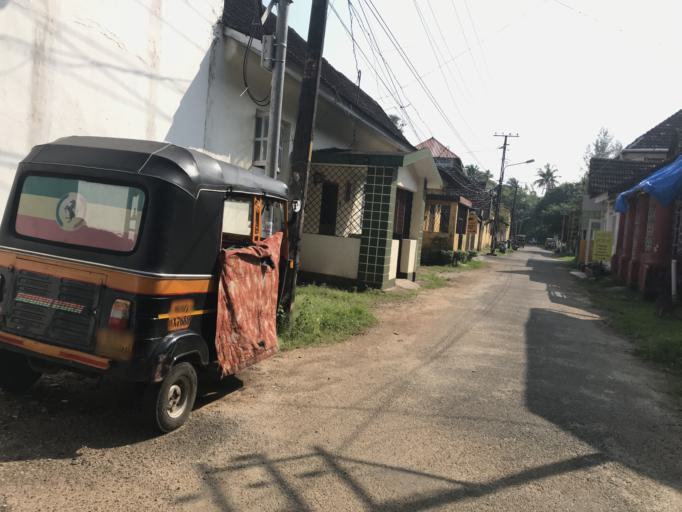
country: IN
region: Kerala
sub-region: Ernakulam
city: Cochin
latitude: 9.9642
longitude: 76.2399
